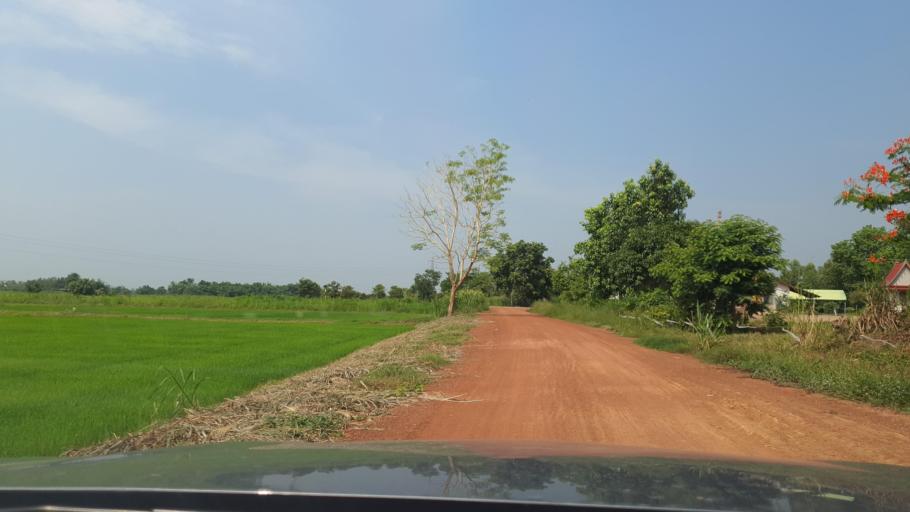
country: TH
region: Phitsanulok
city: Bang Rakam
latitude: 16.7817
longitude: 100.1041
